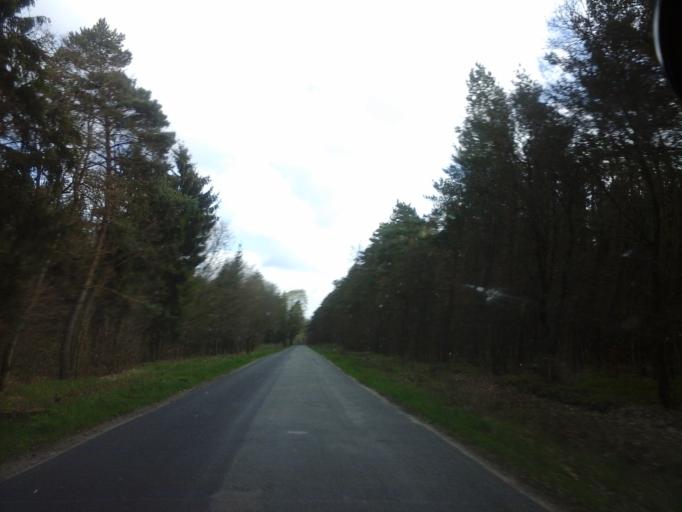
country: PL
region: Lubusz
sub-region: Powiat strzelecko-drezdenecki
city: Dobiegniew
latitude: 53.0602
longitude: 15.7614
